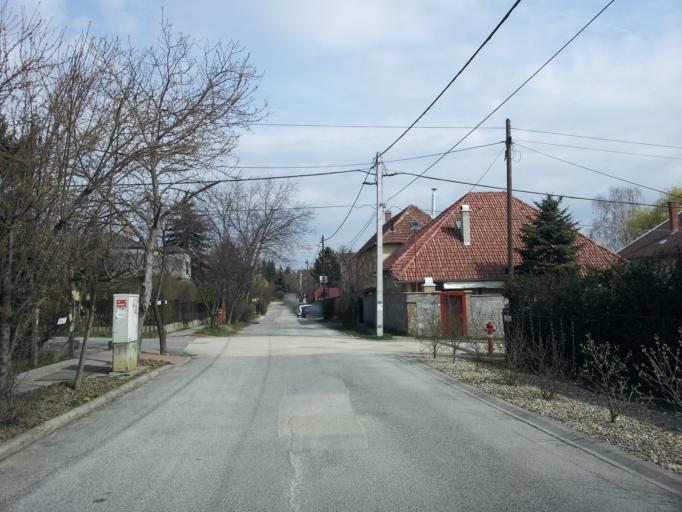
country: HU
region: Pest
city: Budaors
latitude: 47.4641
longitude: 18.9710
